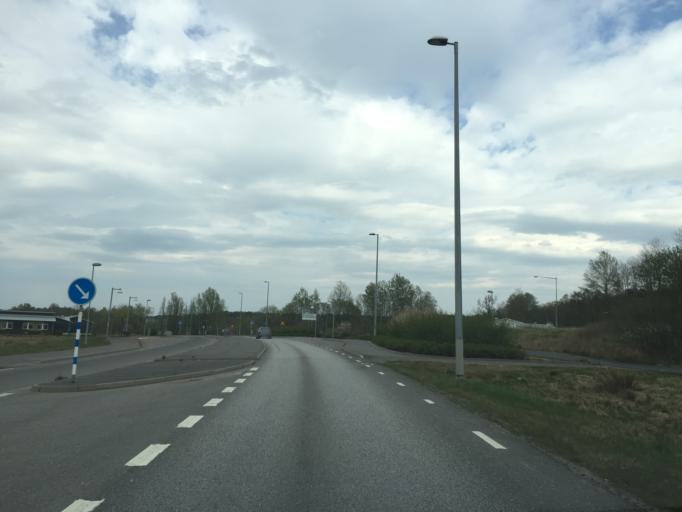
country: SE
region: Vaestra Goetaland
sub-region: Goteborg
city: Loevgaerdet
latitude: 57.8042
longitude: 12.0435
